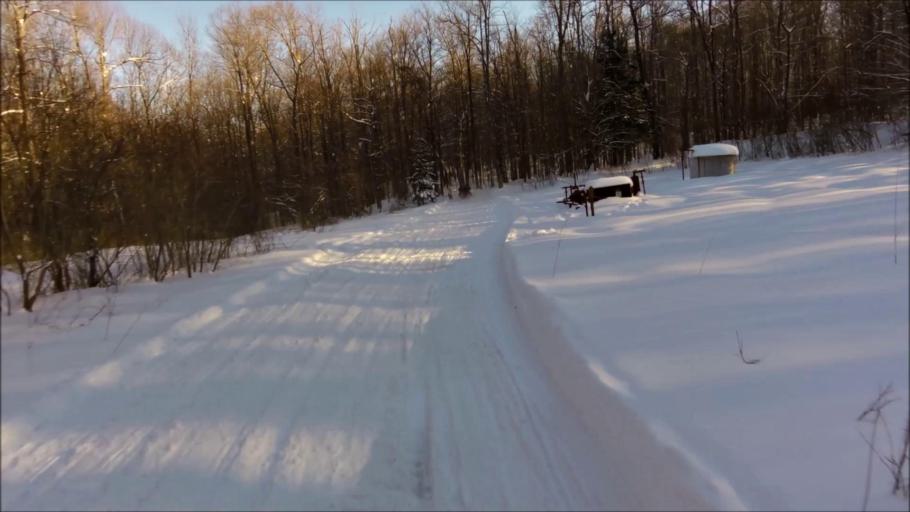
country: US
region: New York
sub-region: Chautauqua County
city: Mayville
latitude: 42.2764
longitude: -79.3898
